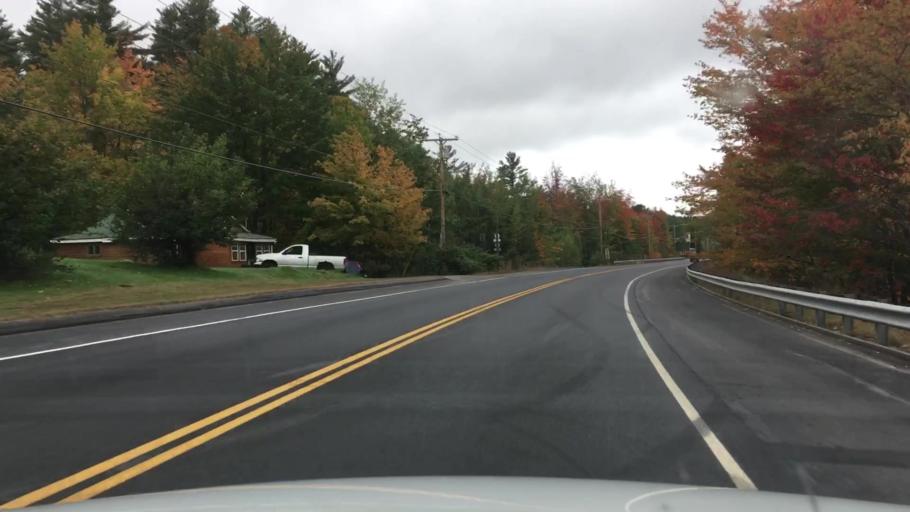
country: US
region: Maine
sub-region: Oxford County
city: Bethel
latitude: 44.4095
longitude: -70.8064
